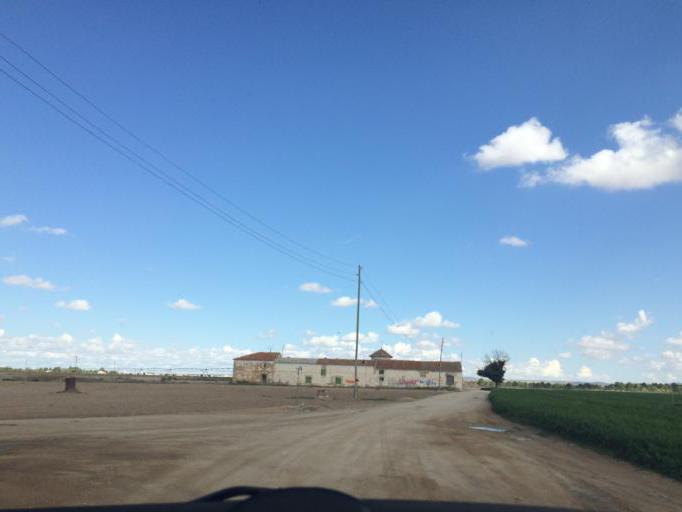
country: ES
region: Castille-La Mancha
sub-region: Provincia de Albacete
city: Albacete
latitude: 38.9588
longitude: -1.8630
